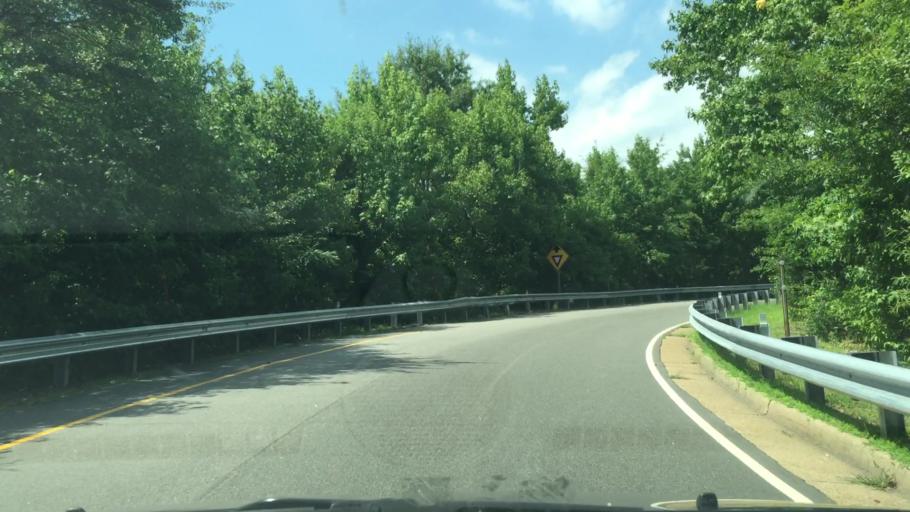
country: US
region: Virginia
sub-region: City of Portsmouth
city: Portsmouth
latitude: 36.8368
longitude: -76.3297
